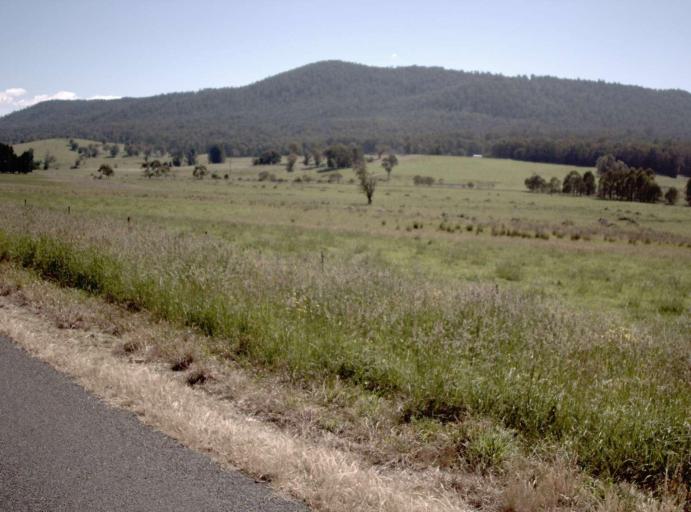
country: AU
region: New South Wales
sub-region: Bombala
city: Bombala
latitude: -37.1937
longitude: 148.7265
